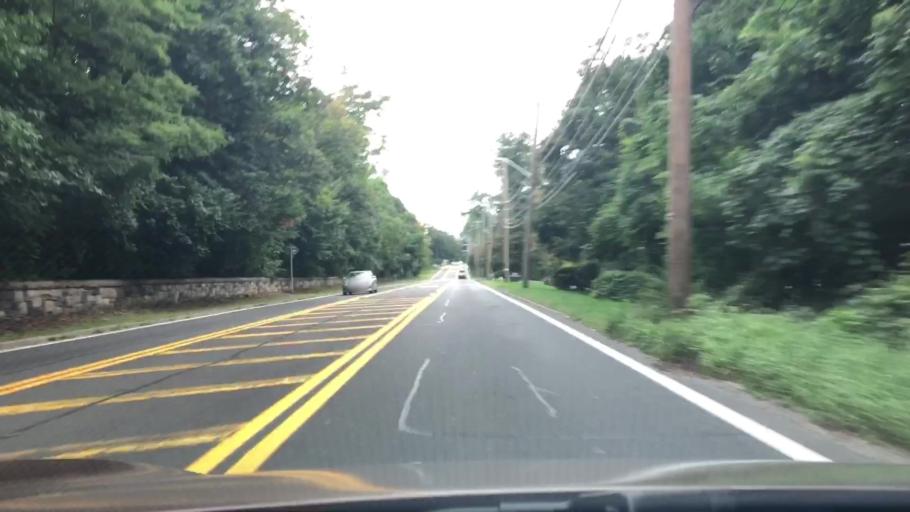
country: US
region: New York
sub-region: Westchester County
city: Ossining
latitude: 41.1281
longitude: -73.8617
